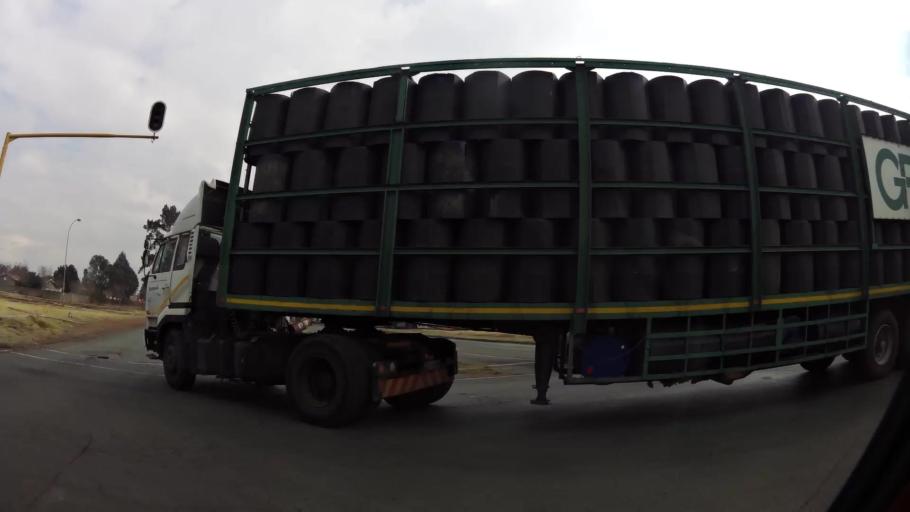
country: ZA
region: Gauteng
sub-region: Sedibeng District Municipality
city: Vanderbijlpark
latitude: -26.6740
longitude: 27.8374
